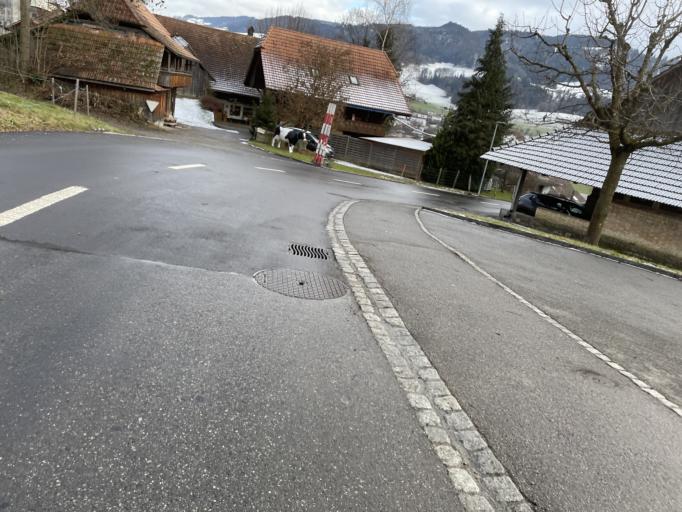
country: CH
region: Lucerne
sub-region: Entlebuch District
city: Oberdiessbach
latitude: 46.8382
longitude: 7.6130
